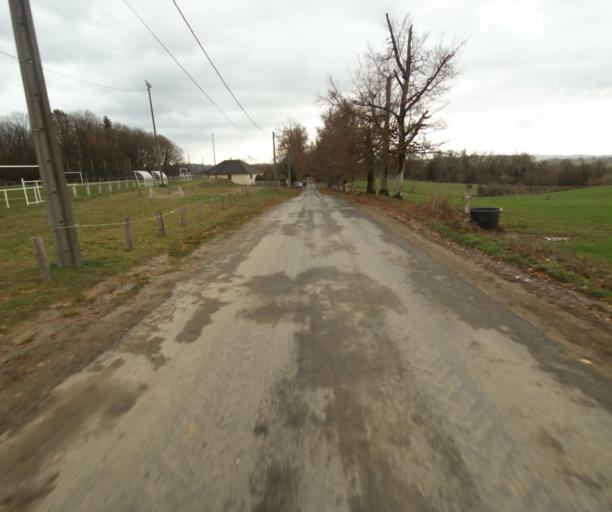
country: FR
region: Limousin
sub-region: Departement de la Correze
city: Saint-Mexant
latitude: 45.2766
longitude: 1.6188
